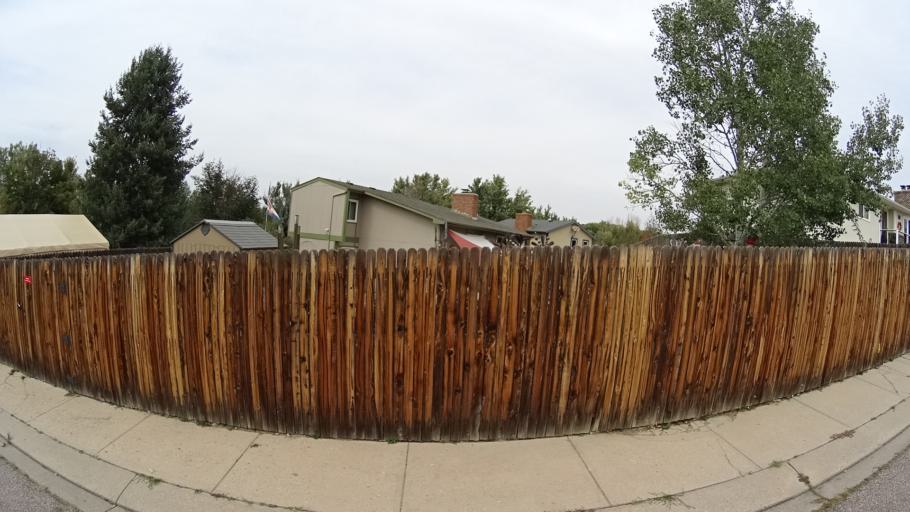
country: US
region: Colorado
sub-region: El Paso County
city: Cimarron Hills
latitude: 38.9003
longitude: -104.7324
